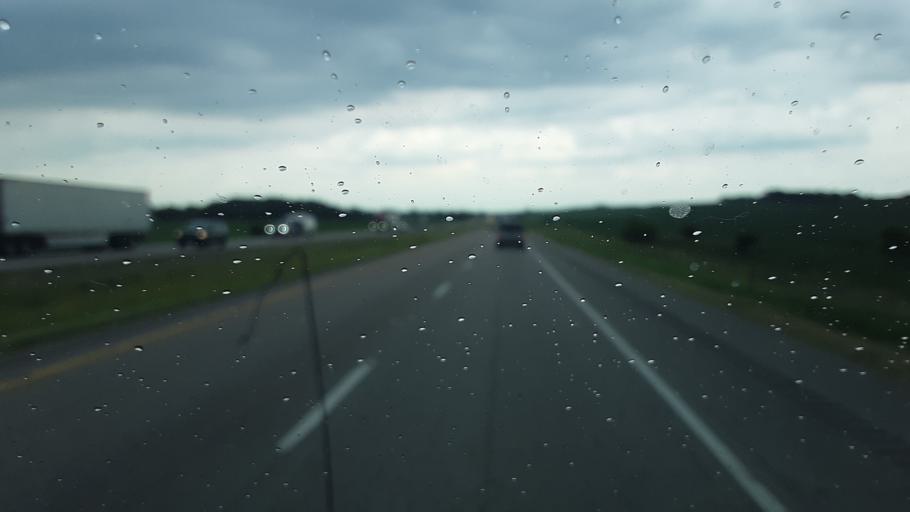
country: US
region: Iowa
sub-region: Pottawattamie County
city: Council Bluffs
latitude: 41.3514
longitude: -95.7008
